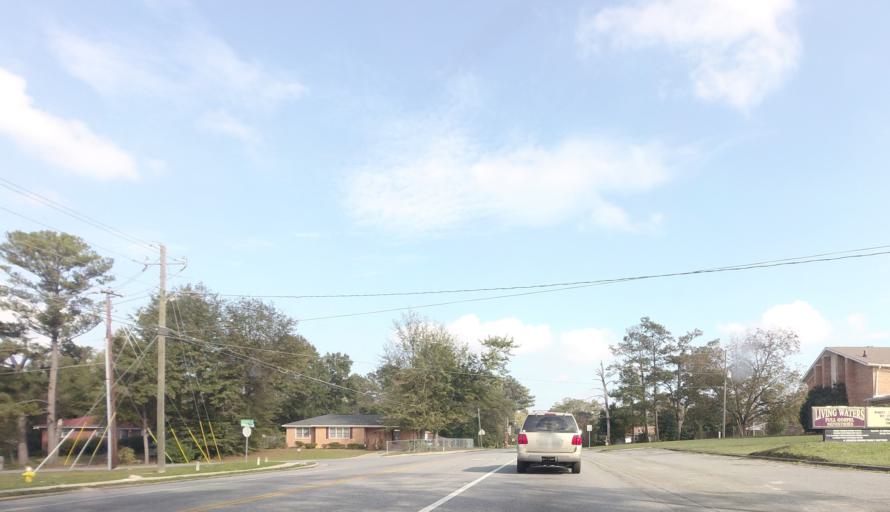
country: US
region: Georgia
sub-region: Bibb County
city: Macon
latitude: 32.8060
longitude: -83.6718
